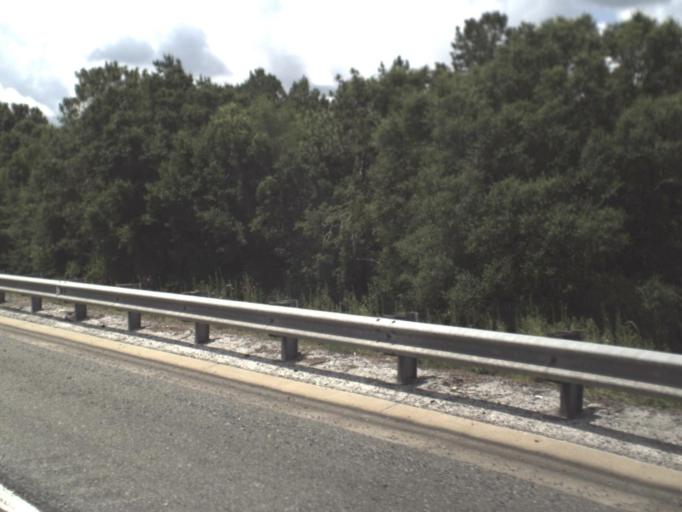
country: US
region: Florida
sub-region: Columbia County
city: Lake City
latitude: 30.2039
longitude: -82.7011
